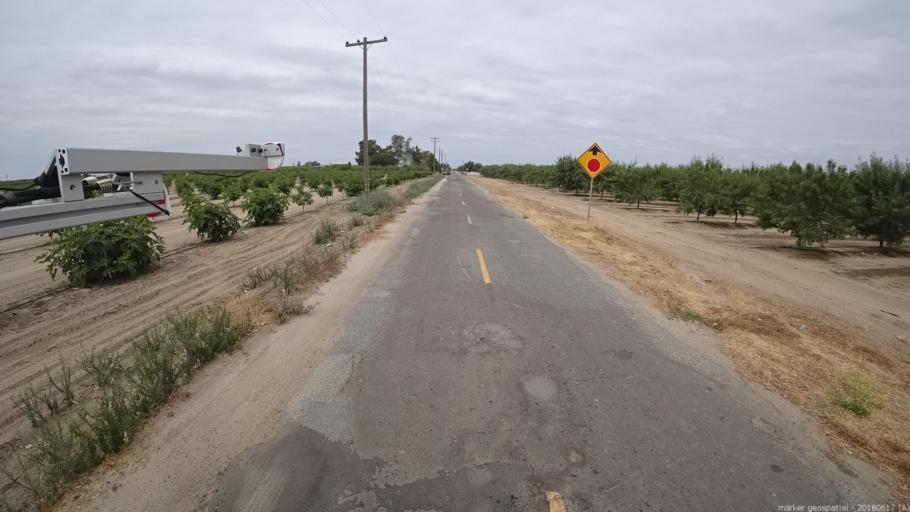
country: US
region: California
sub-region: Madera County
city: Fairmead
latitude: 37.0037
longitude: -120.2006
